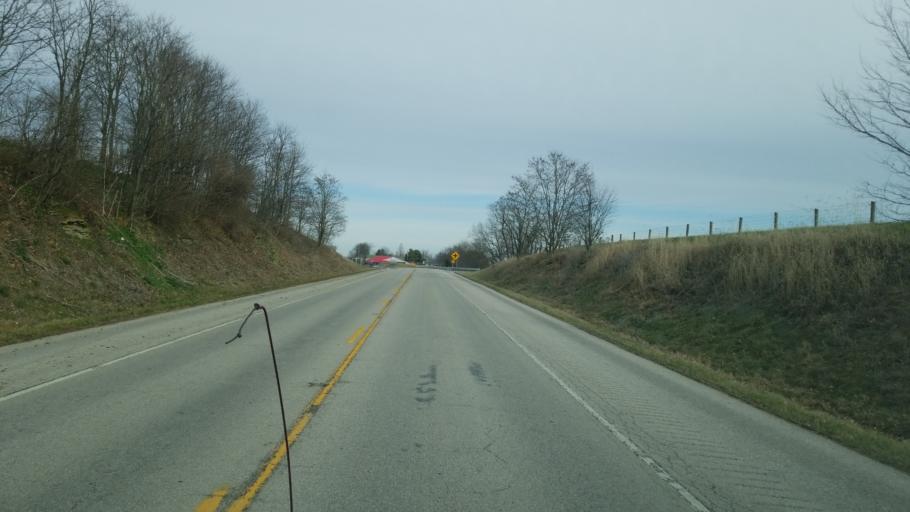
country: US
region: Kentucky
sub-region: Fleming County
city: Flemingsburg
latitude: 38.5142
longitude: -83.8409
